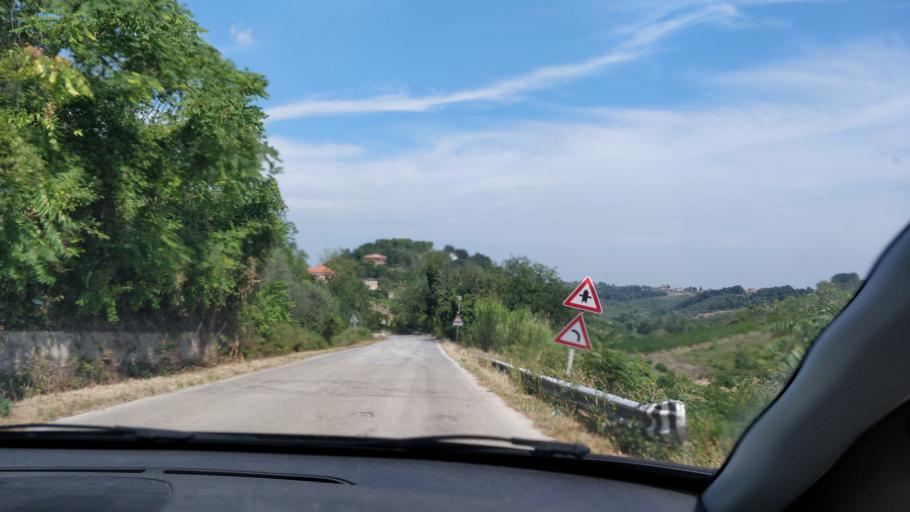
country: IT
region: Abruzzo
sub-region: Provincia di Chieti
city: Torrevecchia
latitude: 42.3993
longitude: 14.2050
